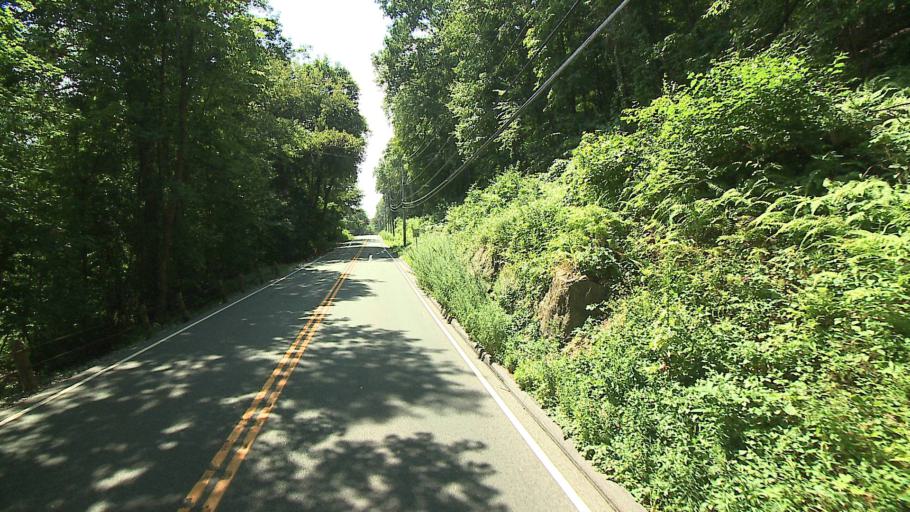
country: US
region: New York
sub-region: Putnam County
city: Putnam Lake
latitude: 41.4861
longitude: -73.4645
